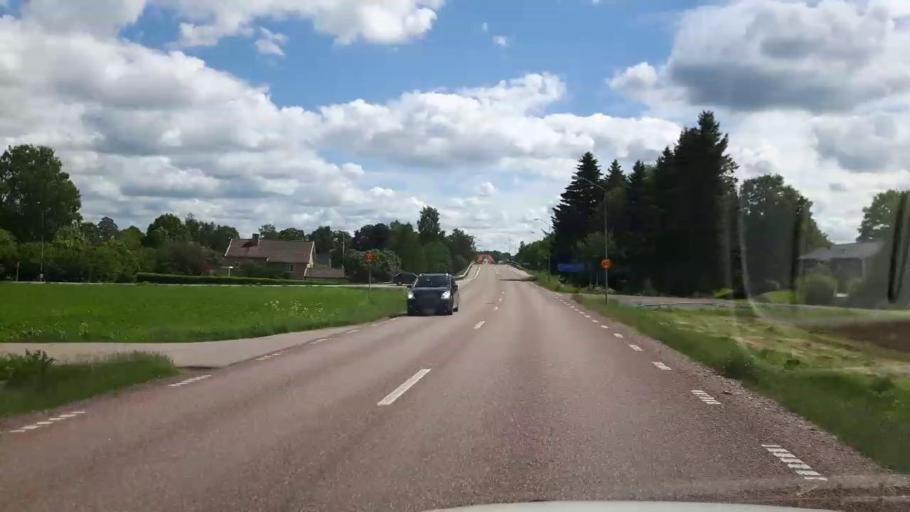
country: SE
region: Dalarna
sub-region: Saters Kommun
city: Saeter
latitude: 60.3981
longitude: 15.8808
